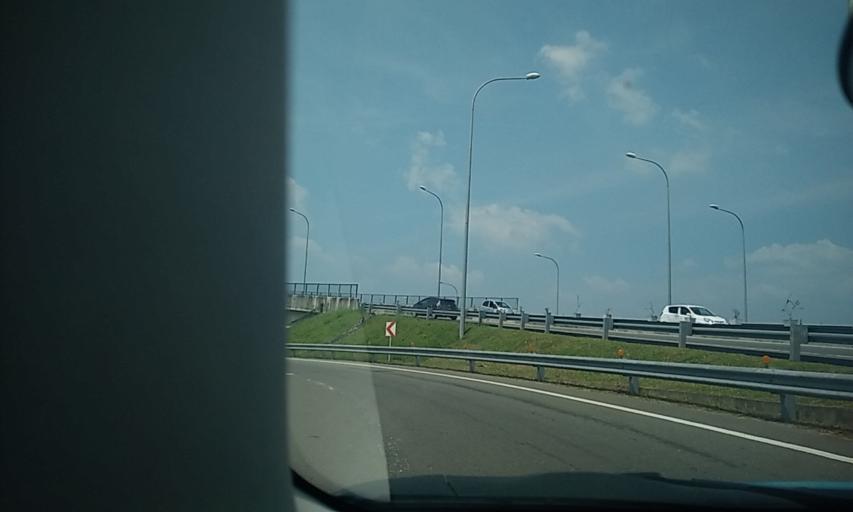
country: LK
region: Western
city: Homagama
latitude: 6.8410
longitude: 79.9816
